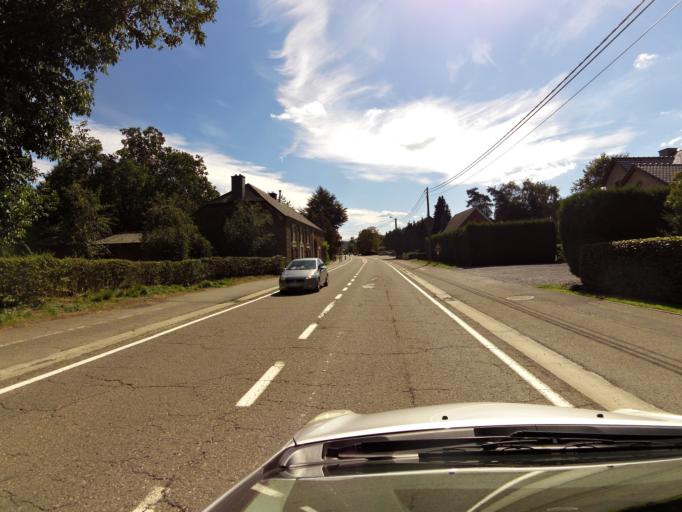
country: BE
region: Wallonia
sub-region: Province du Luxembourg
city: Rendeux
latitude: 50.2412
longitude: 5.5007
